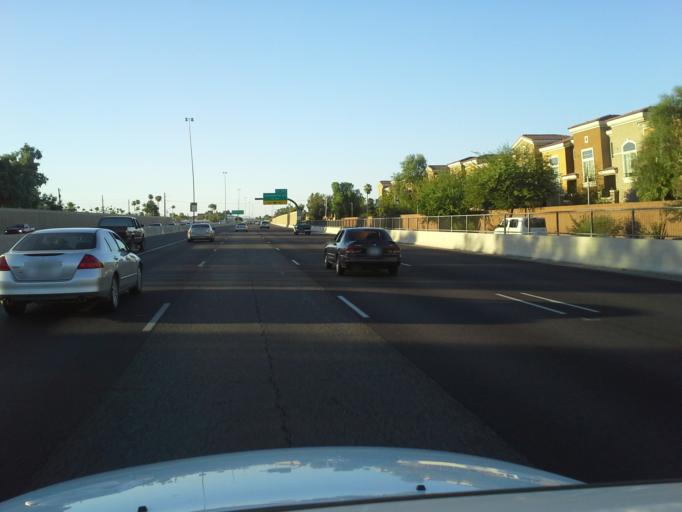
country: US
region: Arizona
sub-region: Maricopa County
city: Phoenix
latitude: 33.4988
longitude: -112.1129
